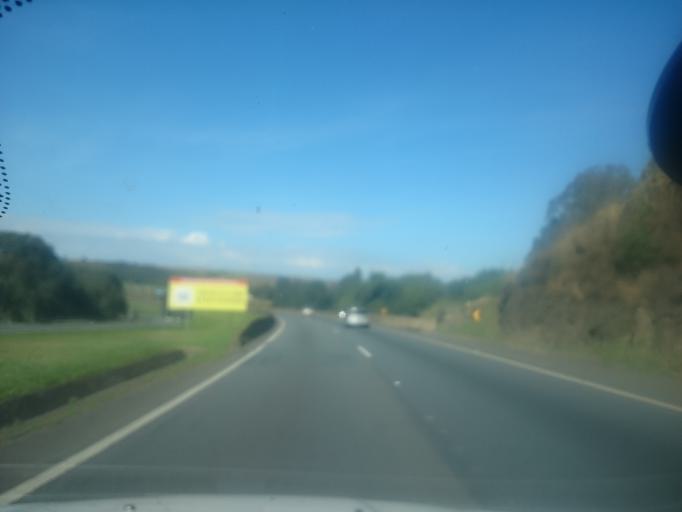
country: BR
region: Parana
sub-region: Campo Largo
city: Campo Largo
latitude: -25.4734
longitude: -49.7232
